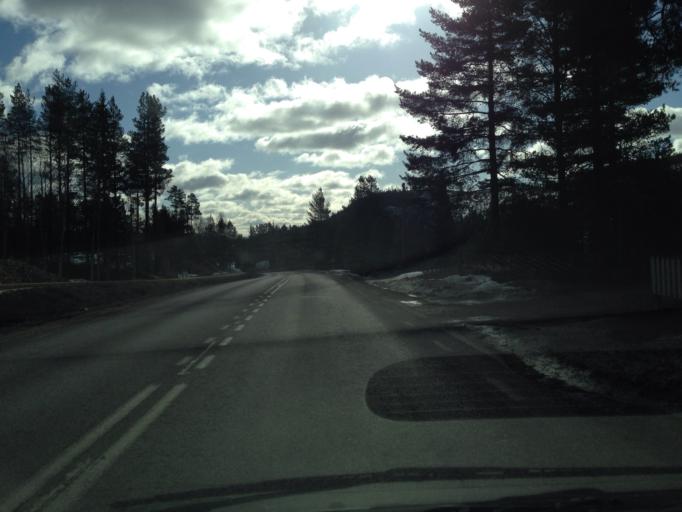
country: SE
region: Gaevleborg
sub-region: Ljusdals Kommun
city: Farila
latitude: 61.9823
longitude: 15.3148
